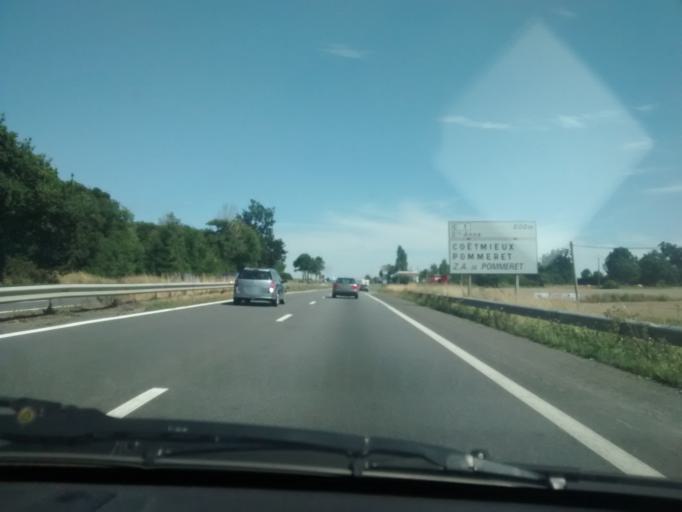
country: FR
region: Brittany
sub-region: Departement des Cotes-d'Armor
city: Pommeret
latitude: 48.4800
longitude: -2.6290
